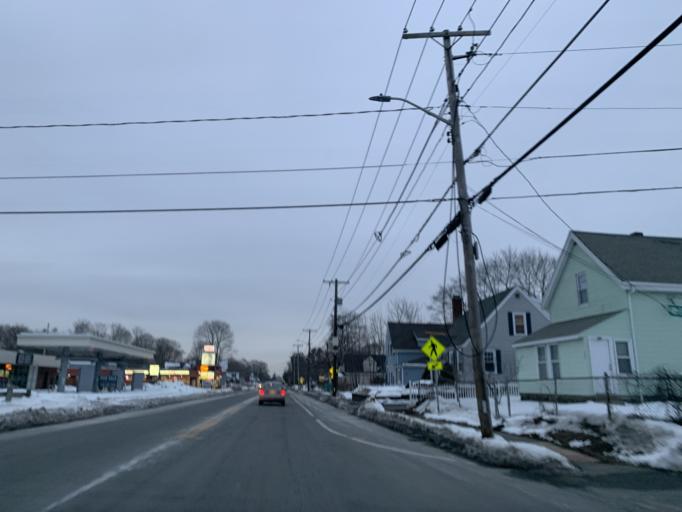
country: US
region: Massachusetts
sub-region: Norfolk County
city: Stoughton
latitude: 42.1202
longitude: -71.0907
